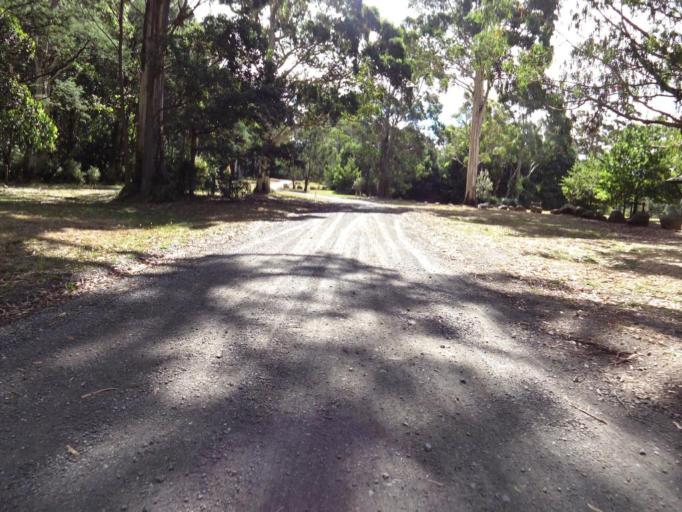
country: AU
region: Victoria
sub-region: Hume
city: Sunbury
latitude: -37.3716
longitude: 144.6071
